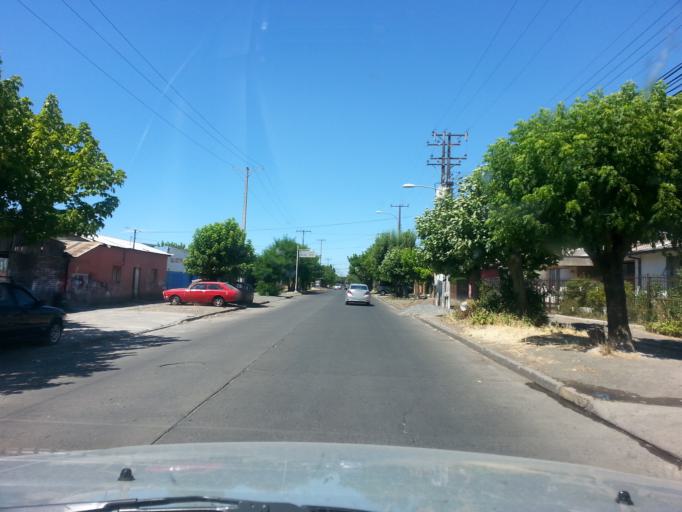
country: CL
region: Biobio
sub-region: Provincia de Nuble
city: Chillan
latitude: -36.6060
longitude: -72.0851
